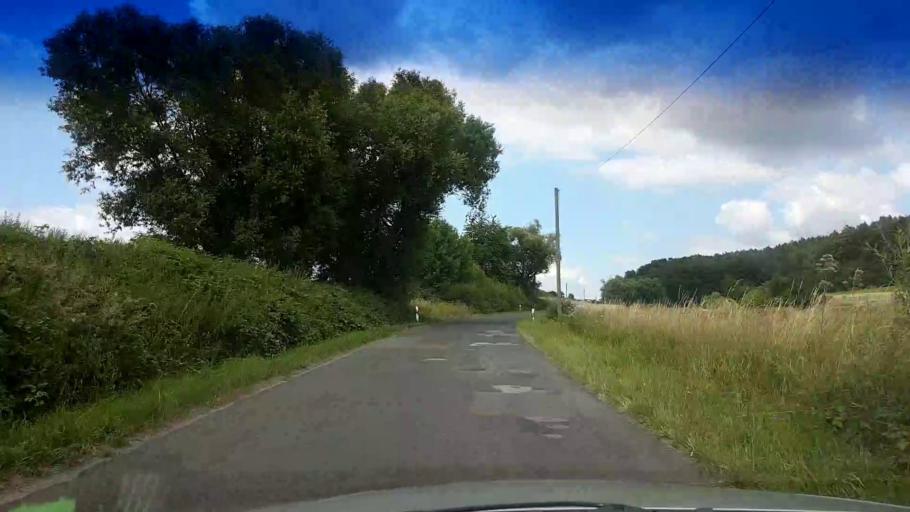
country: DE
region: Bavaria
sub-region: Upper Franconia
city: Lauter
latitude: 49.9926
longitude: 10.7619
